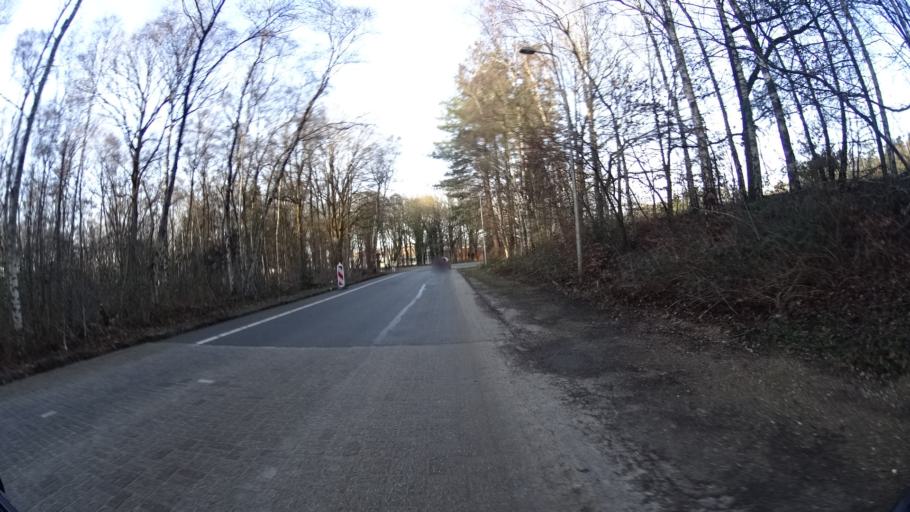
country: NL
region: Gelderland
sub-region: Gemeente Ede
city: Ede
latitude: 52.0321
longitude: 5.6787
